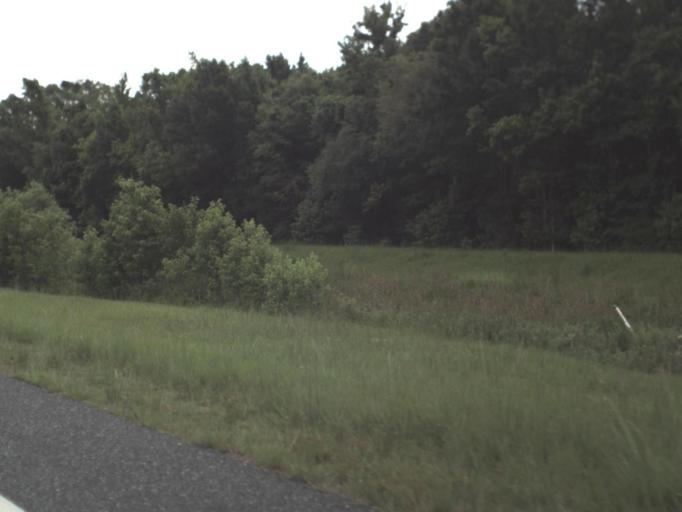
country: US
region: Florida
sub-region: Levy County
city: Williston Highlands
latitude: 29.2575
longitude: -82.7257
